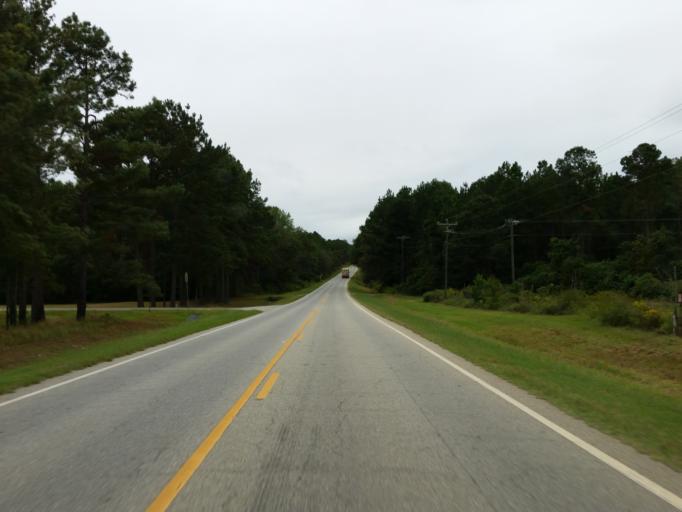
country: US
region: Georgia
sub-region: Cook County
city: Adel
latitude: 31.1314
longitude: -83.3645
